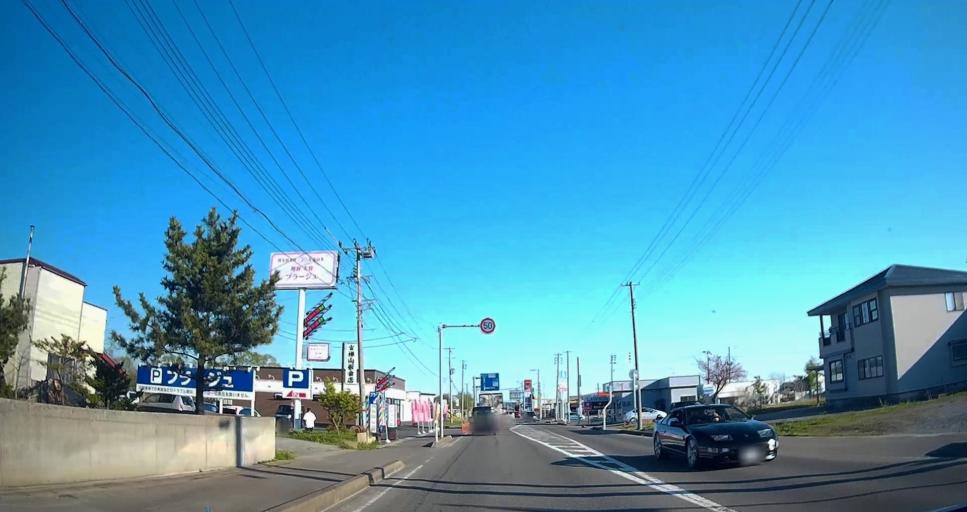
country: JP
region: Aomori
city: Mutsu
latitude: 41.3061
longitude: 141.2195
